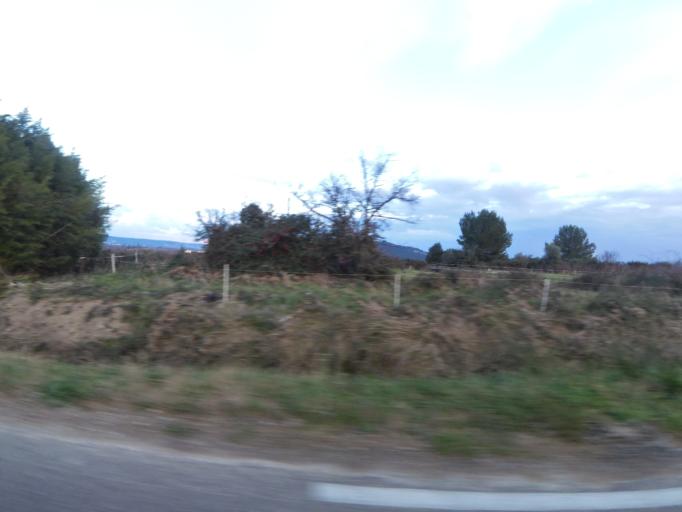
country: FR
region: Languedoc-Roussillon
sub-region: Departement du Gard
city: Calvisson
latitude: 43.7936
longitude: 4.1949
